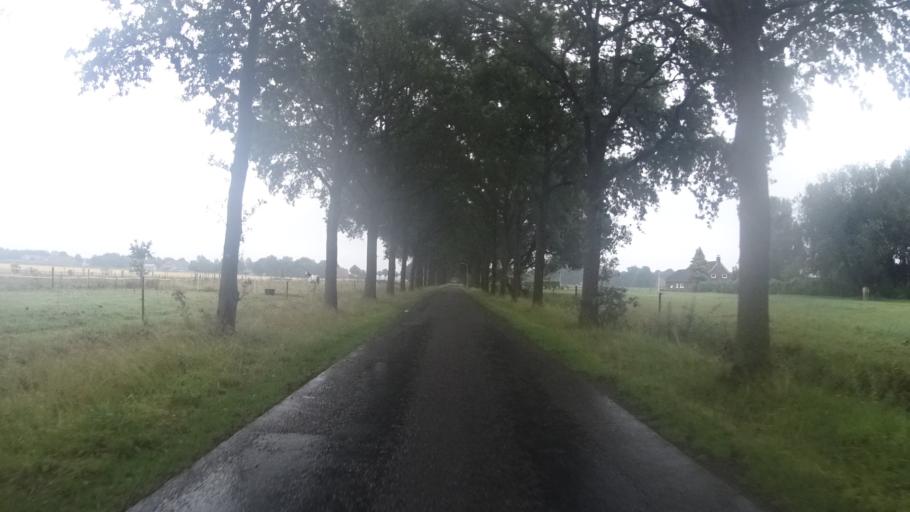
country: NL
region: Groningen
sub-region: Gemeente Slochteren
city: Slochteren
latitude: 53.1791
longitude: 6.8649
